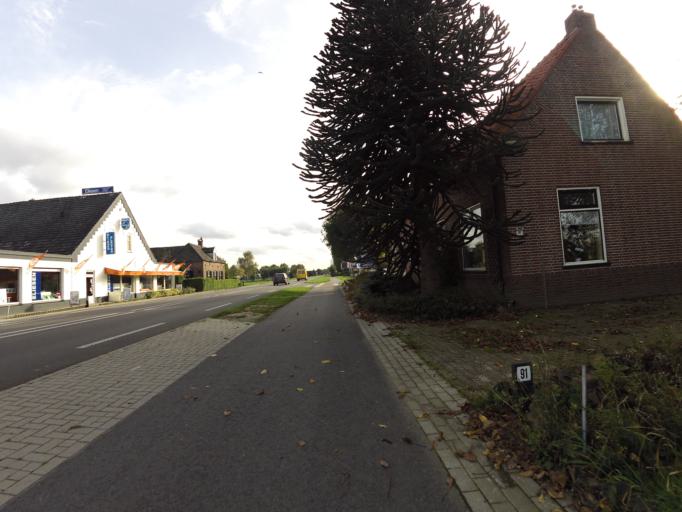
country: NL
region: Gelderland
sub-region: Gemeente Bronckhorst
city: Baak
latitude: 52.0637
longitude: 6.2235
